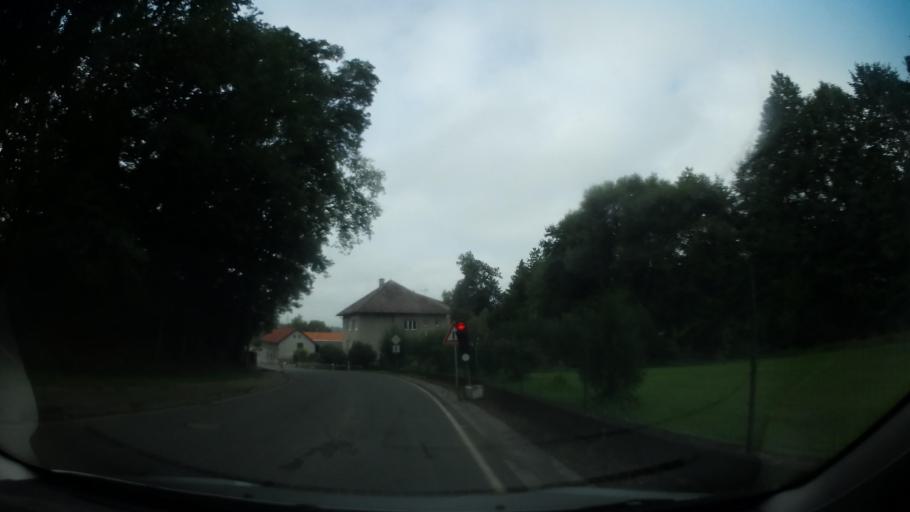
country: CZ
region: Central Bohemia
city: Neveklov
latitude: 49.7221
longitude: 14.4794
